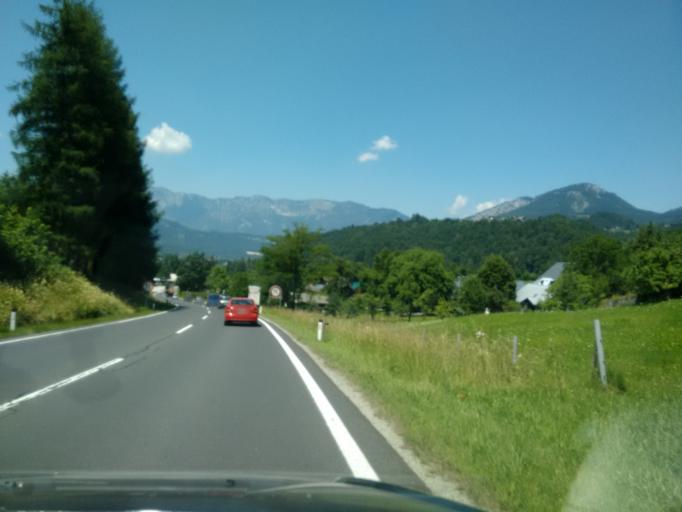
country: AT
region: Upper Austria
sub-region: Politischer Bezirk Gmunden
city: Bad Goisern
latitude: 47.6197
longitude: 13.6517
